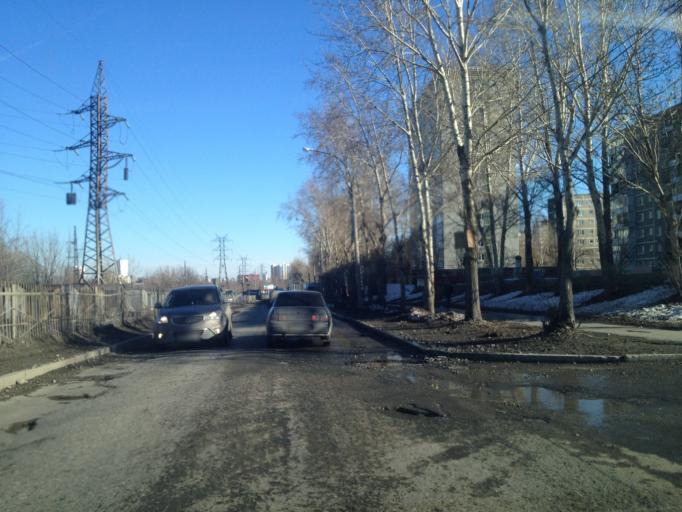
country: RU
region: Sverdlovsk
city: Yekaterinburg
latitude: 56.8722
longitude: 60.5598
